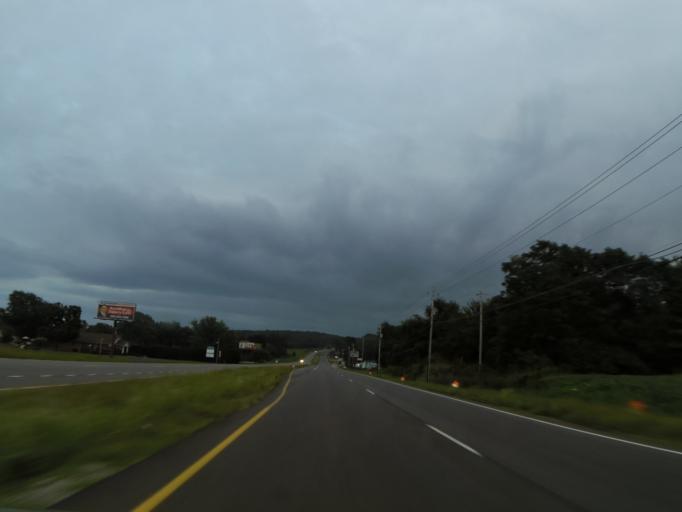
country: US
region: Alabama
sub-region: Madison County
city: Moores Mill
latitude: 34.7714
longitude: -86.5070
